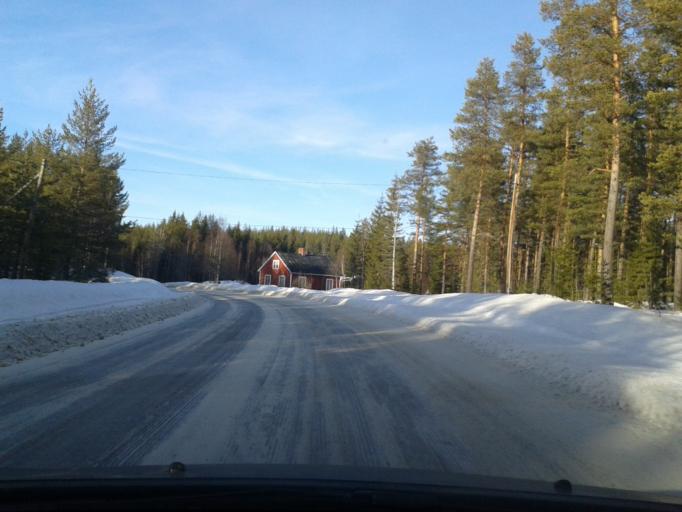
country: SE
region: Vaesternorrland
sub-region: OErnskoeldsviks Kommun
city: Bredbyn
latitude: 63.7391
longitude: 17.7451
